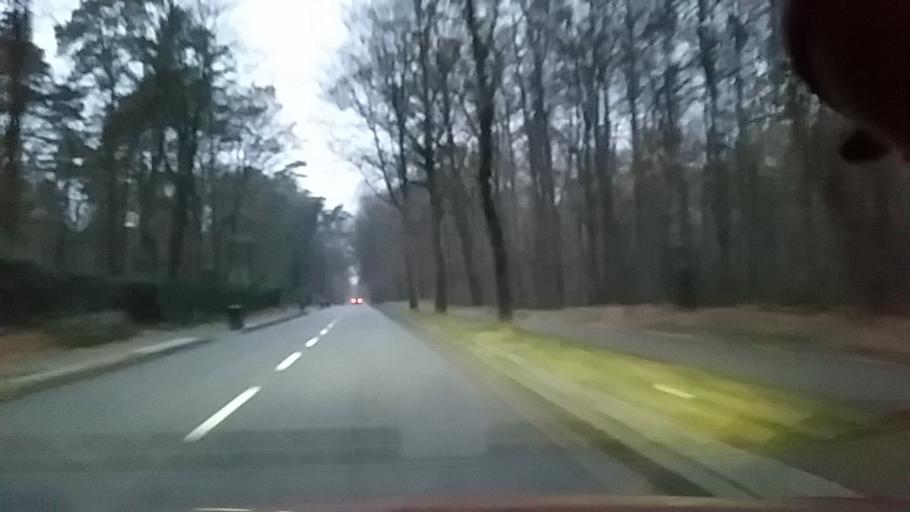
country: DE
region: Schleswig-Holstein
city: Wedel
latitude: 53.5750
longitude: 9.7803
